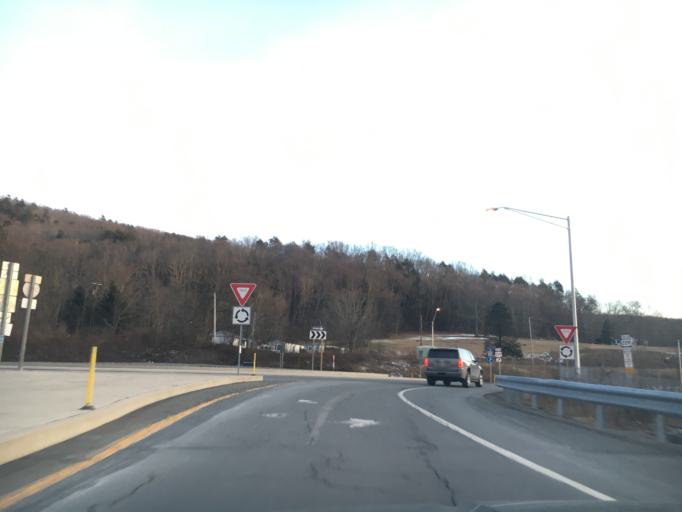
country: US
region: Pennsylvania
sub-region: Monroe County
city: East Stroudsburg
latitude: 41.0343
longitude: -75.1240
